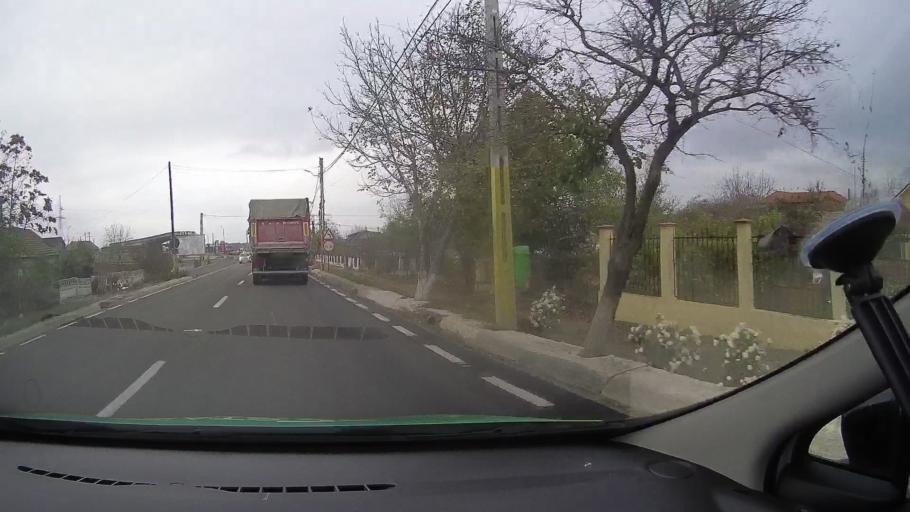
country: RO
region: Constanta
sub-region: Comuna Poarta Alba
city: Poarta Alba
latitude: 44.2111
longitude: 28.3946
